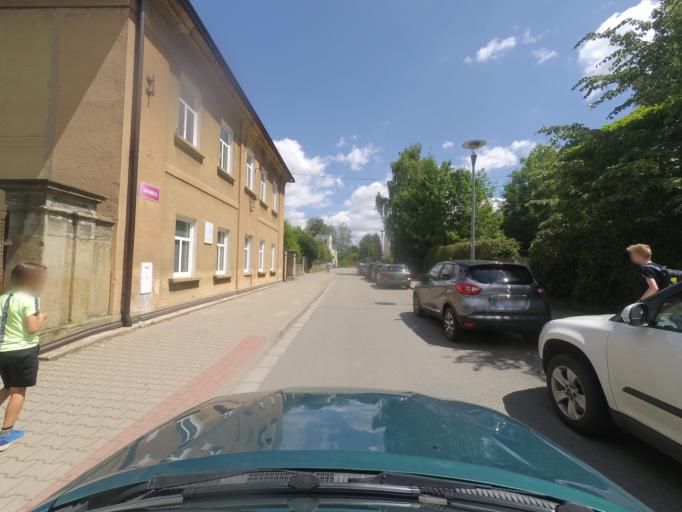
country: CZ
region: Kralovehradecky
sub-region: Okres Rychnov nad Kneznou
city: Rychnov nad Kneznou
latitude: 50.1642
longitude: 16.2778
